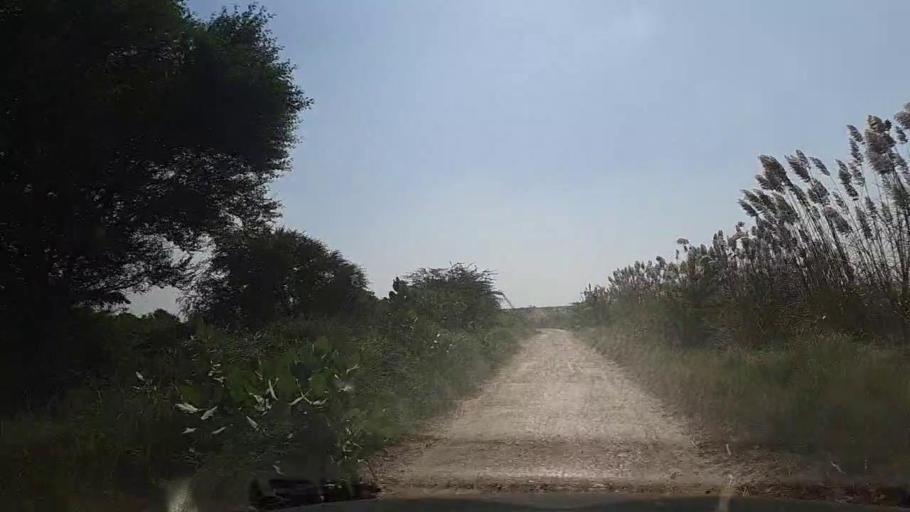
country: PK
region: Sindh
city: Daro Mehar
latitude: 24.8301
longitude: 68.0886
